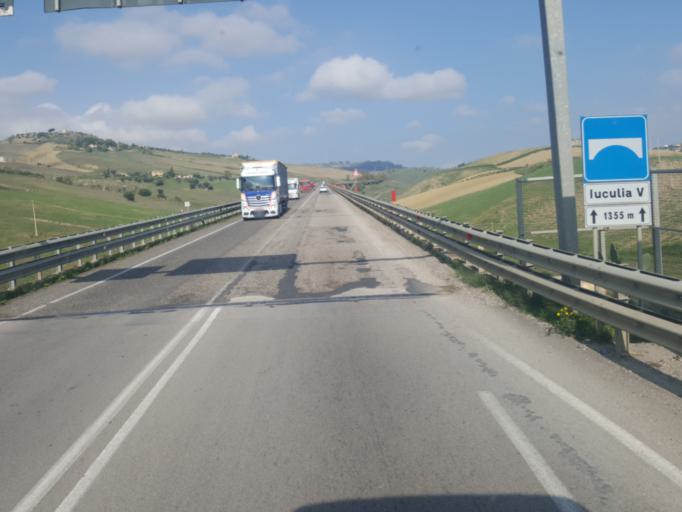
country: IT
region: Sicily
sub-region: Enna
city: Pietraperzia
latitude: 37.4583
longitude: 14.1063
